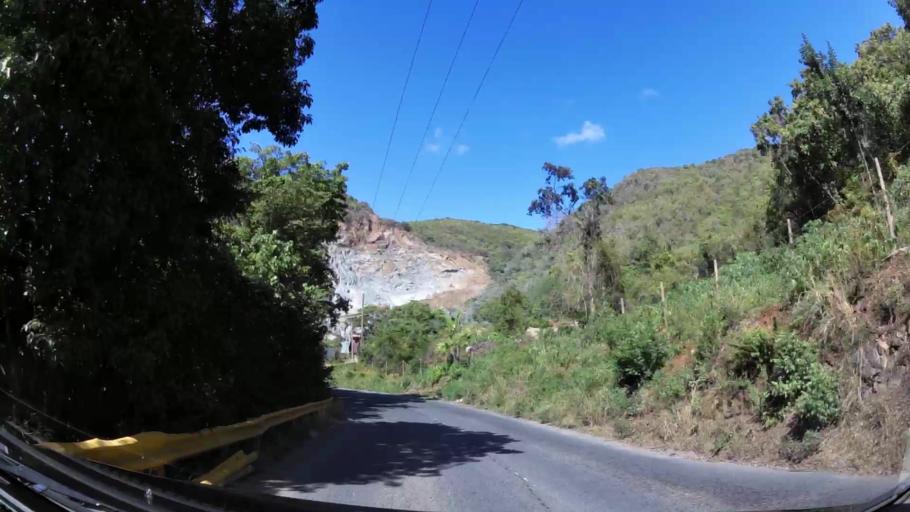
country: VG
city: Tortola
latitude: 18.4187
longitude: -64.5975
